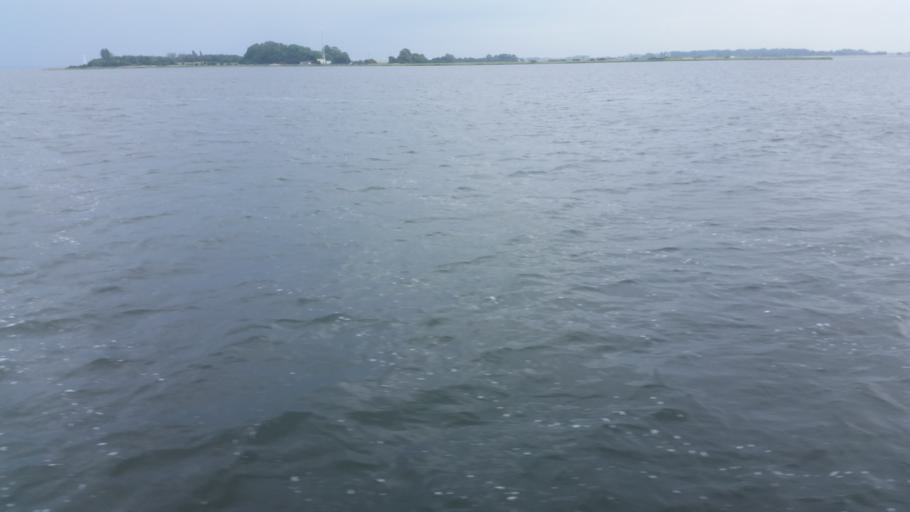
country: DE
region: Mecklenburg-Vorpommern
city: Hiddensee
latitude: 54.5435
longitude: 13.1314
